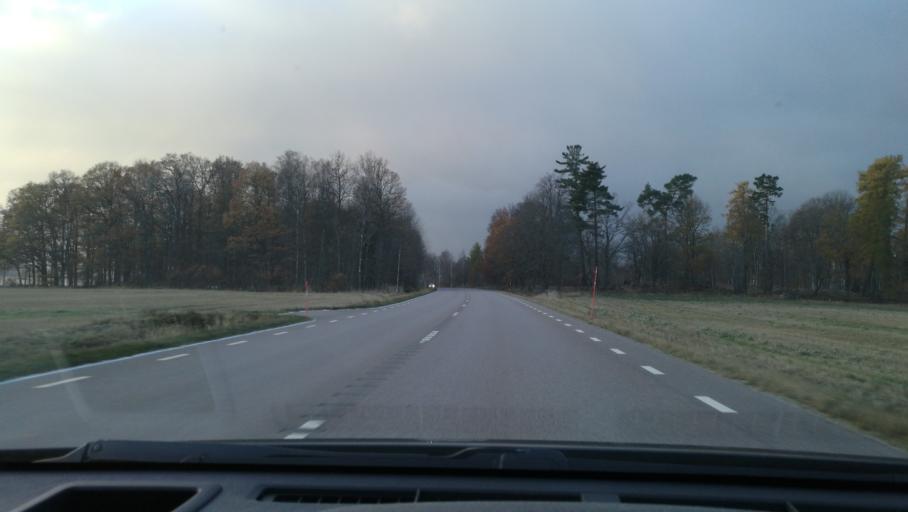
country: SE
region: Soedermanland
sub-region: Vingakers Kommun
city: Vingaker
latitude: 59.1571
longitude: 16.0267
